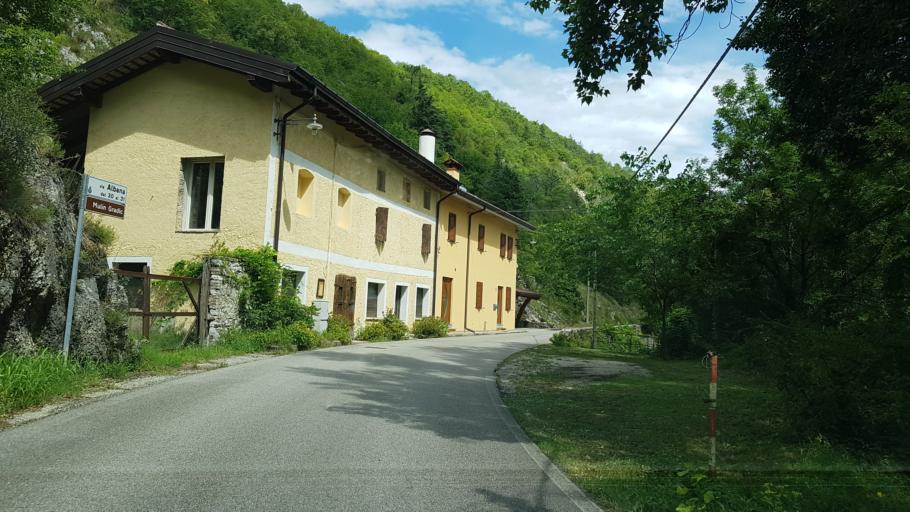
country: IT
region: Friuli Venezia Giulia
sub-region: Provincia di Udine
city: Prepotto
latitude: 46.0626
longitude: 13.5022
